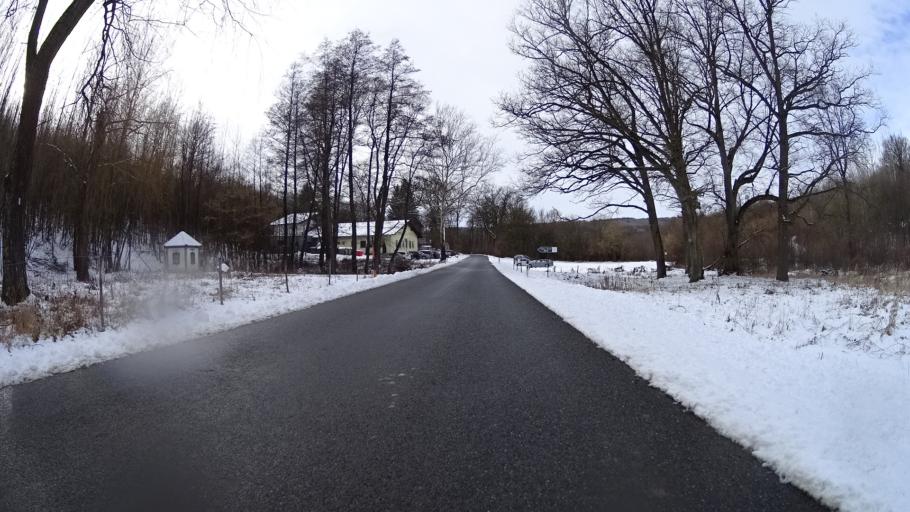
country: AT
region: Lower Austria
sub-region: Politischer Bezirk Korneuburg
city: Niederhollabrunn
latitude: 48.4131
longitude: 16.3168
